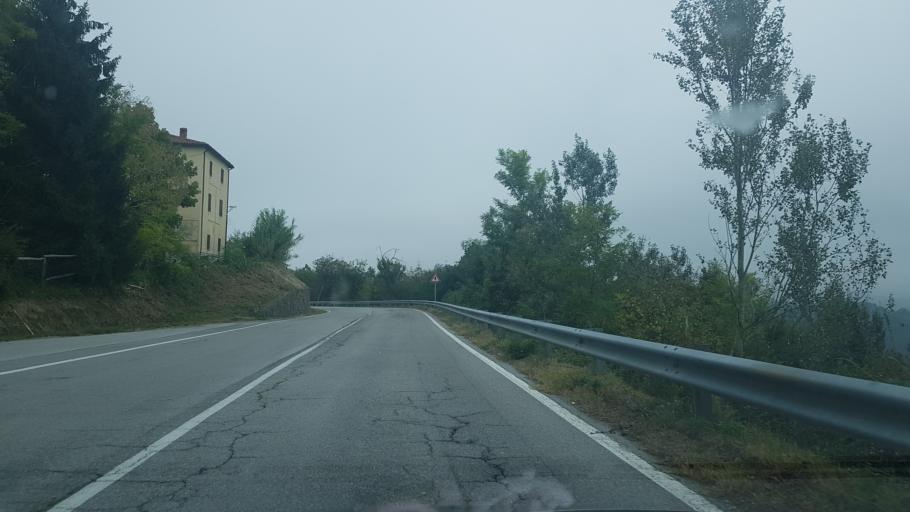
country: IT
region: Piedmont
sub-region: Provincia di Cuneo
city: Sale delle Langhe
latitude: 44.4060
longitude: 8.1089
